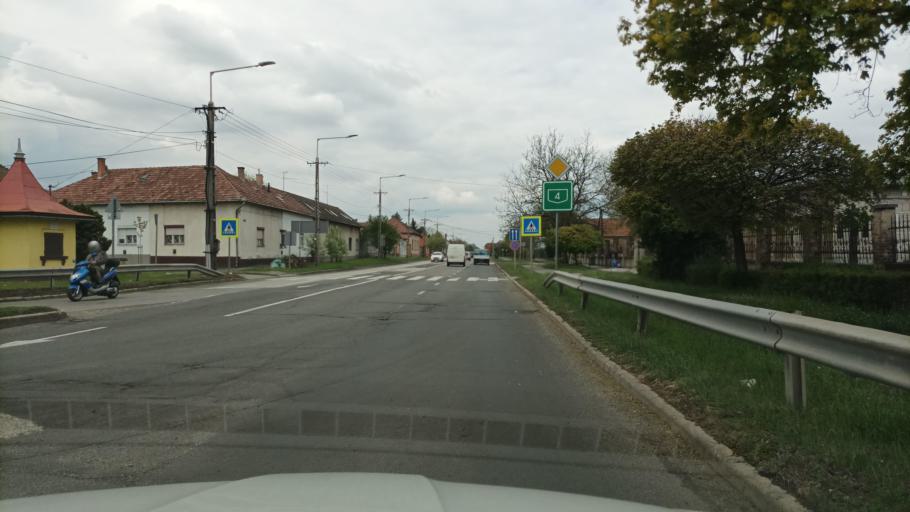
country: HU
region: Pest
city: Cegled
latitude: 47.1728
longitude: 19.8131
